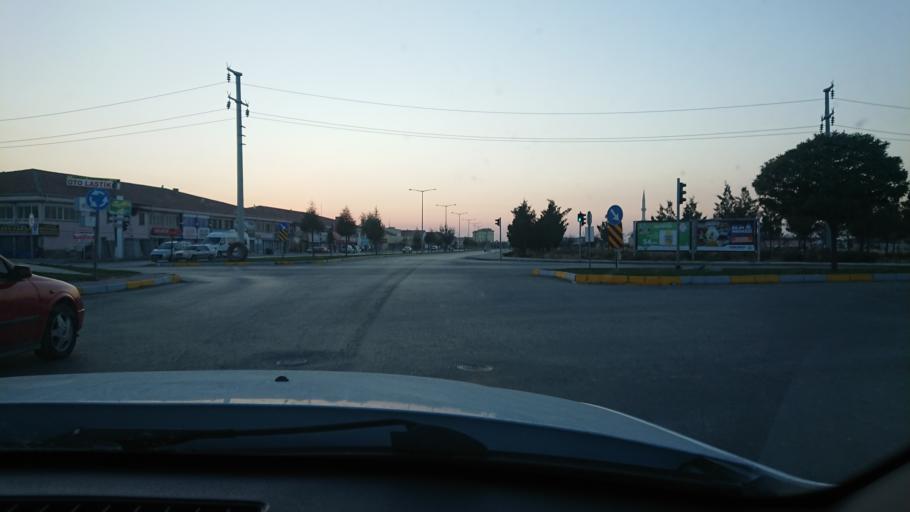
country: TR
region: Aksaray
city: Aksaray
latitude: 38.3573
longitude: 33.9896
